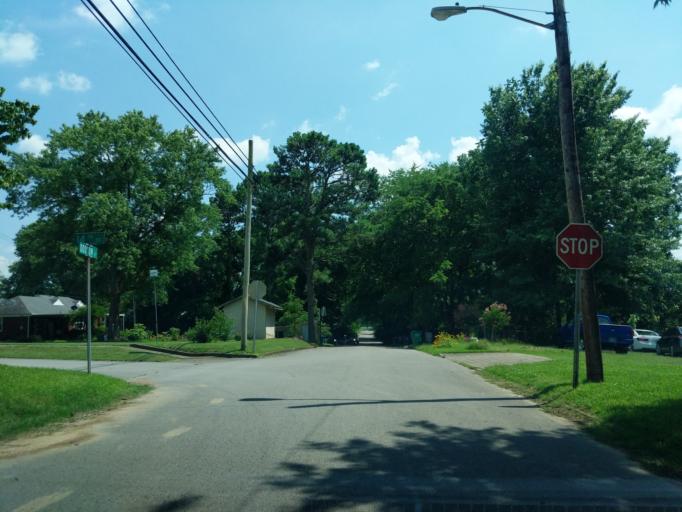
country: US
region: Tennessee
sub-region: Davidson County
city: Lakewood
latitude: 36.2567
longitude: -86.6485
